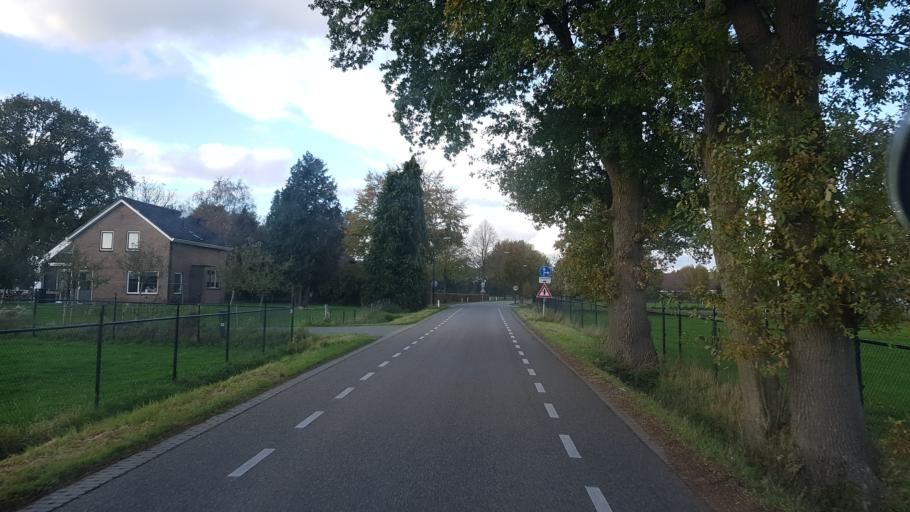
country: NL
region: Gelderland
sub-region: Gemeente Apeldoorn
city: Beekbergen
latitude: 52.1688
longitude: 5.9816
